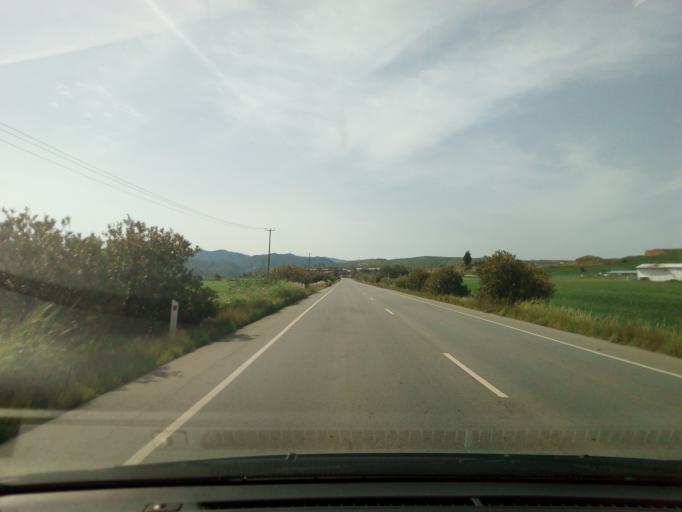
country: CY
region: Lefkosia
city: Klirou
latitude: 35.0329
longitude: 33.1678
